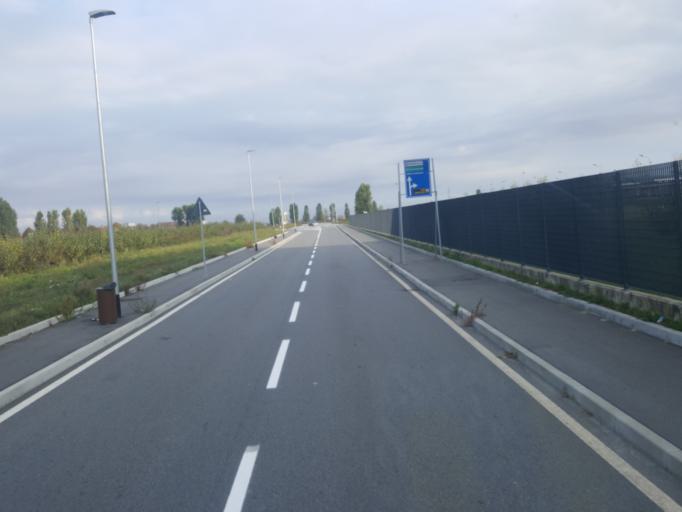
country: IT
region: Piedmont
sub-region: Provincia di Vercelli
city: Asigliano Vercellese
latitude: 45.2934
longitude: 8.3906
